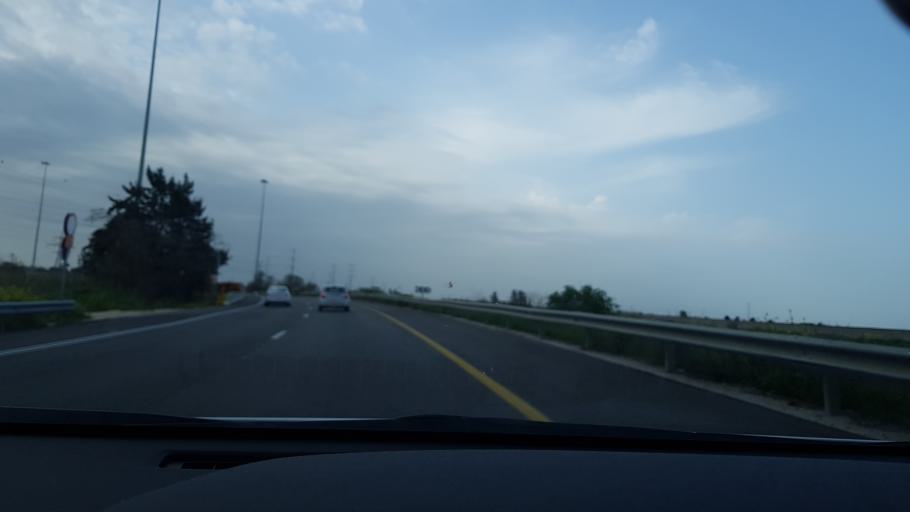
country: IL
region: Central District
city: Gan Yavne
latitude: 31.8126
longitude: 34.6963
